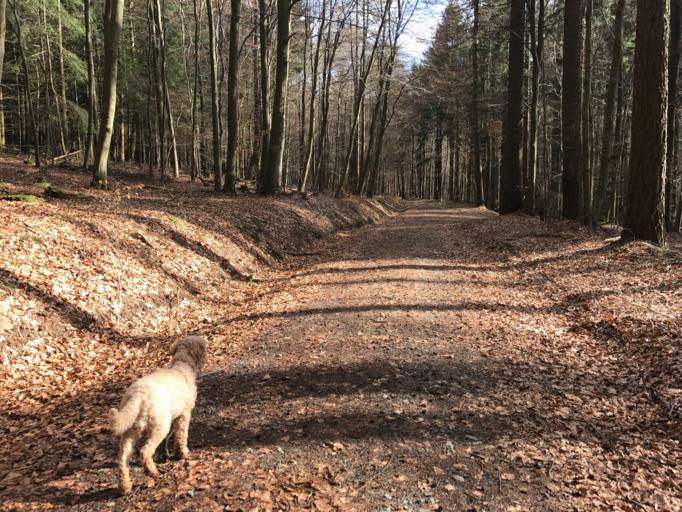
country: DE
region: Hesse
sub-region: Regierungsbezirk Darmstadt
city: Konigstein im Taunus
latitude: 50.2045
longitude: 8.4436
